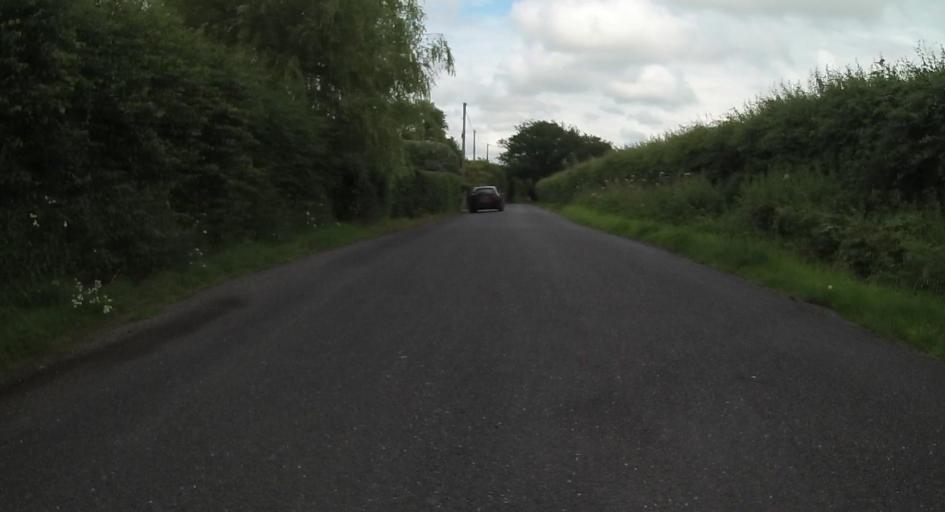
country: GB
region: England
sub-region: Hampshire
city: Kingsley
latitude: 51.1767
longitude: -0.8889
